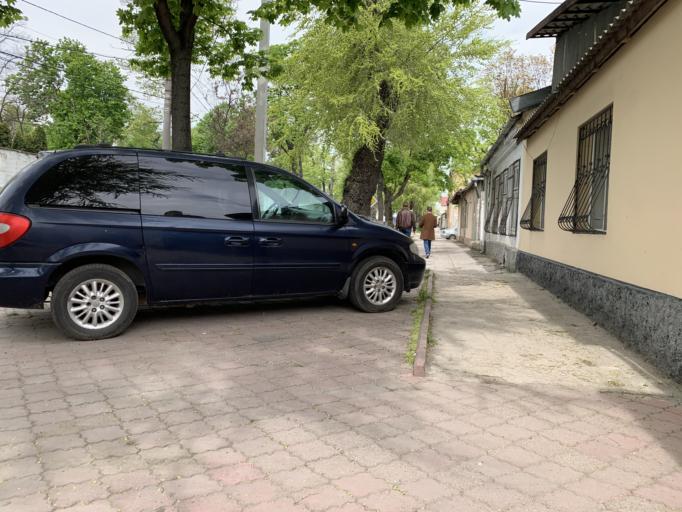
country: MD
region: Chisinau
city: Chisinau
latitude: 47.0115
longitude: 28.8324
